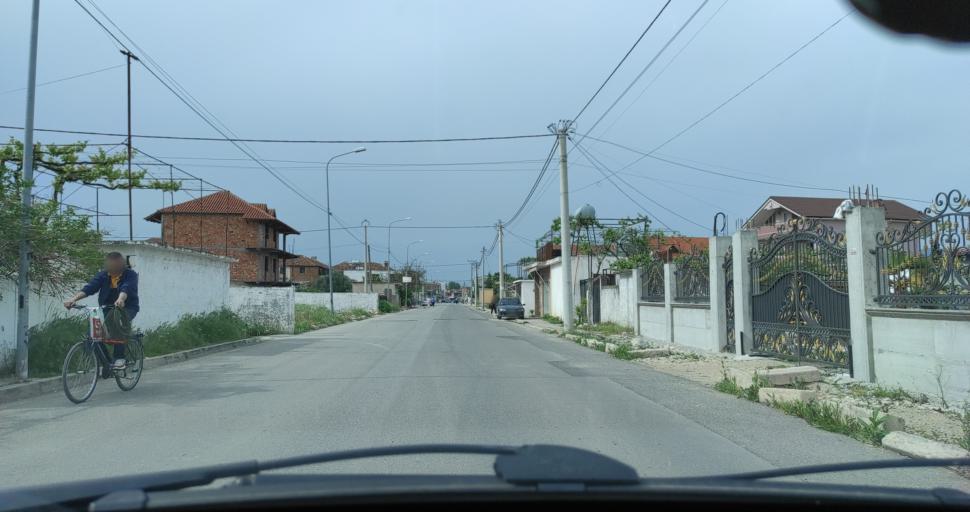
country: AL
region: Durres
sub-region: Rrethi i Krujes
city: Fushe-Kruje
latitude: 41.4744
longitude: 19.7185
